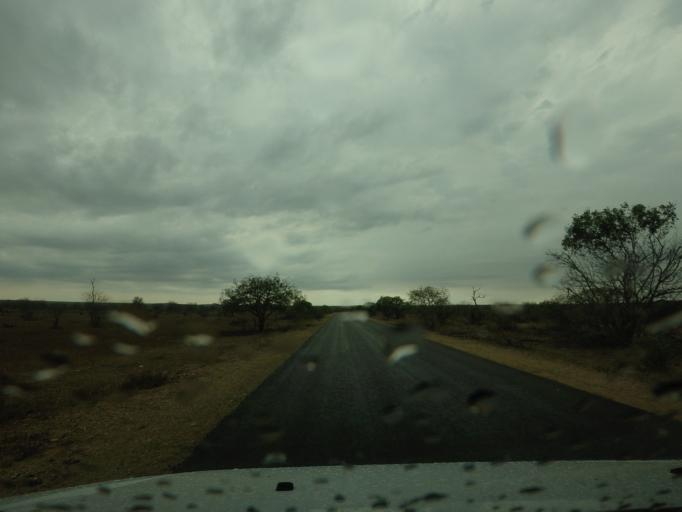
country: ZA
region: Limpopo
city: Thulamahashi
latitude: -24.4741
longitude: 31.4036
